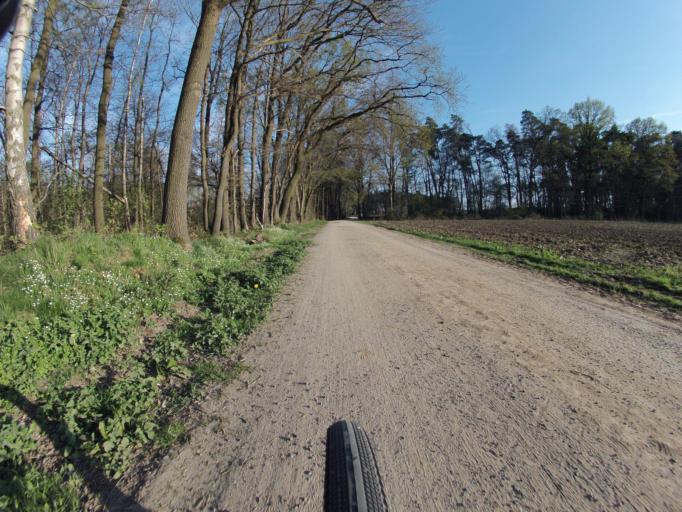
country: DE
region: Lower Saxony
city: Salzbergen
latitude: 52.3511
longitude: 7.3401
